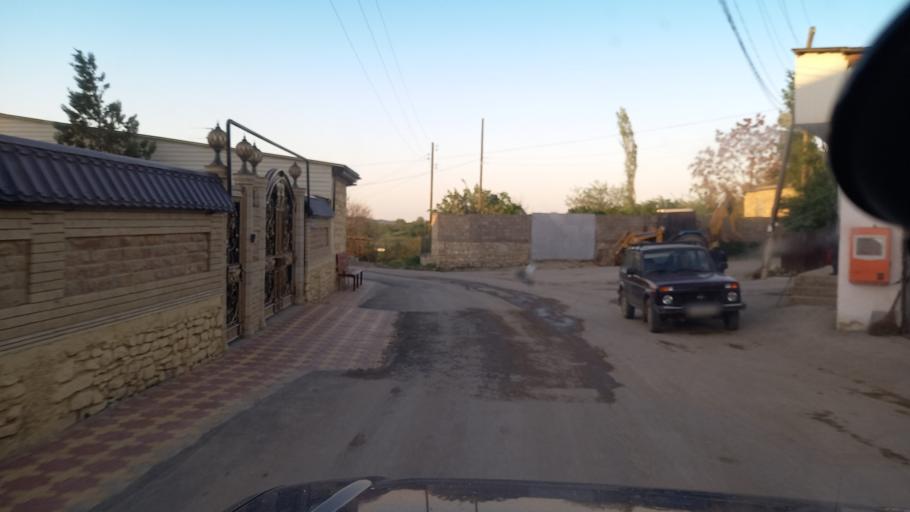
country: RU
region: Dagestan
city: Khuchni
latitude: 42.0236
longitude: 47.9680
